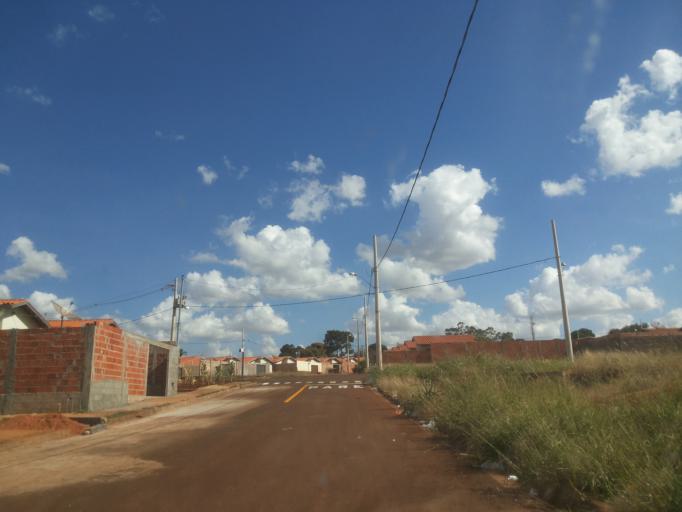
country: BR
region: Minas Gerais
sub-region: Capinopolis
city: Capinopolis
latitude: -18.6851
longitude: -49.5617
